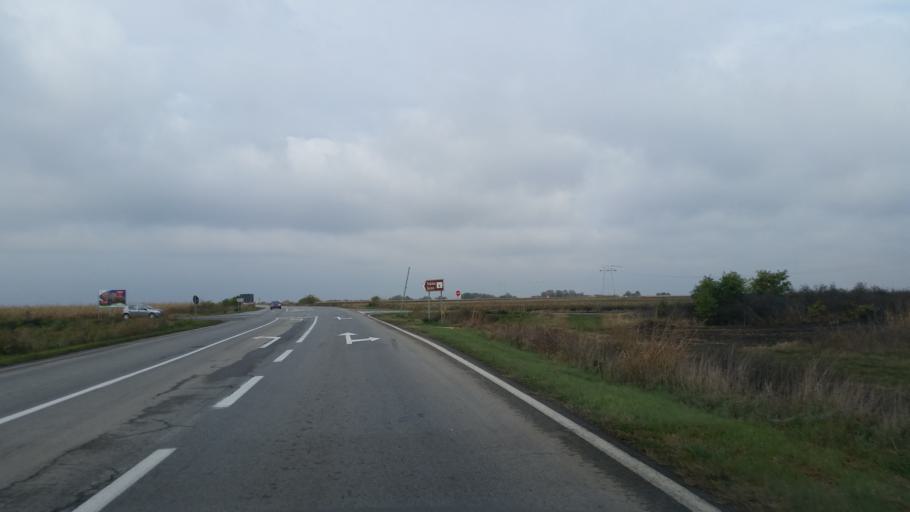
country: RS
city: Elemir
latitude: 45.4591
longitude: 20.3501
